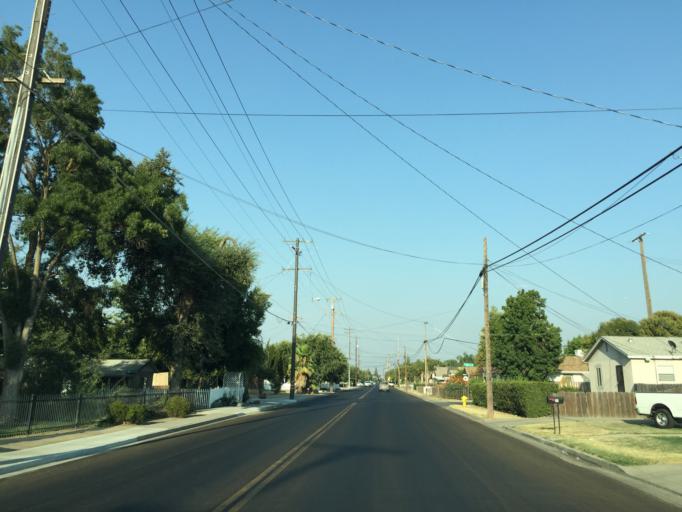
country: US
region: California
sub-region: Tulare County
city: Visalia
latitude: 36.3201
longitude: -119.2859
